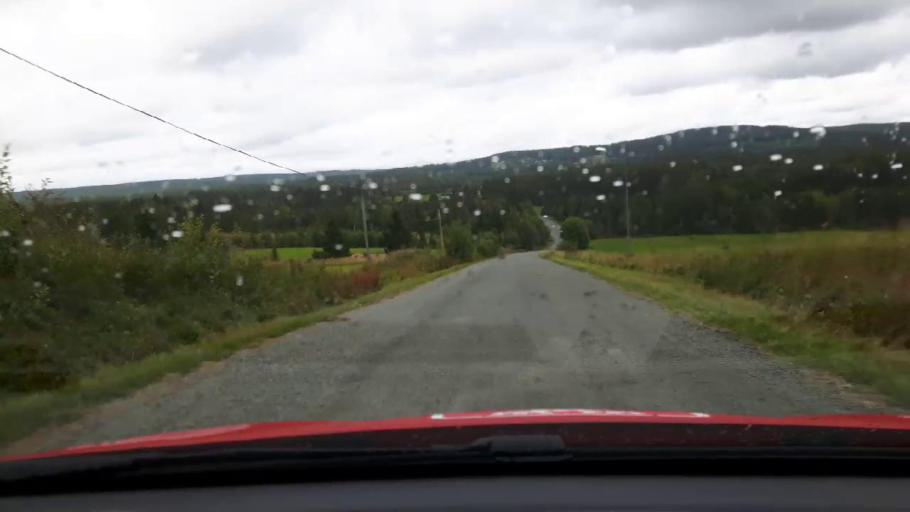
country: SE
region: Jaemtland
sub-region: Bergs Kommun
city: Hoverberg
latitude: 62.8546
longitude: 14.3345
